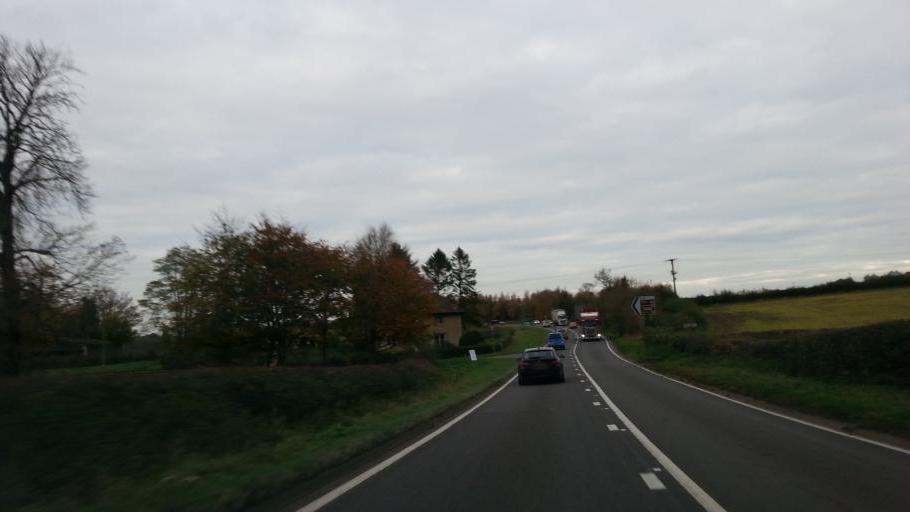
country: GB
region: England
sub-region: District of Rutland
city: Morcott
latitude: 52.5237
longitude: -0.5911
